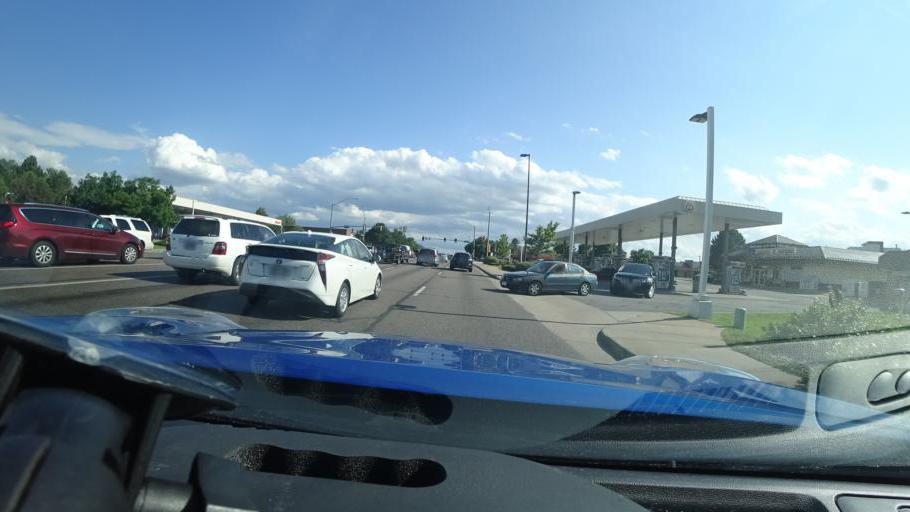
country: US
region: Colorado
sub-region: Adams County
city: Aurora
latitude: 39.6757
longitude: -104.8661
